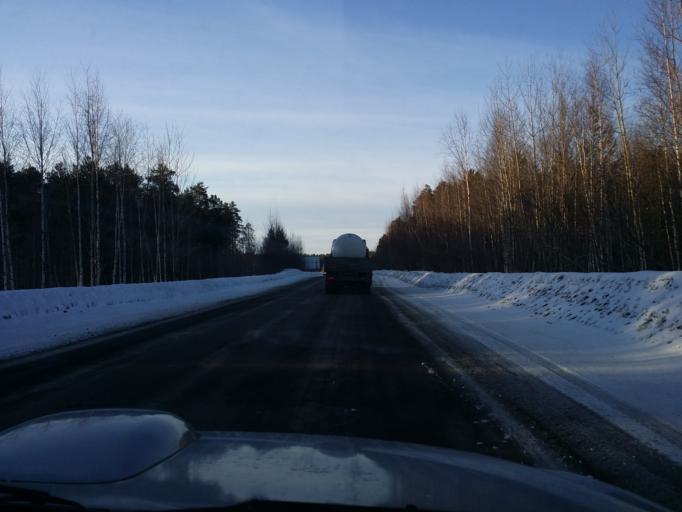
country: RU
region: Khanty-Mansiyskiy Avtonomnyy Okrug
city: Izluchinsk
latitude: 60.9406
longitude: 76.8600
